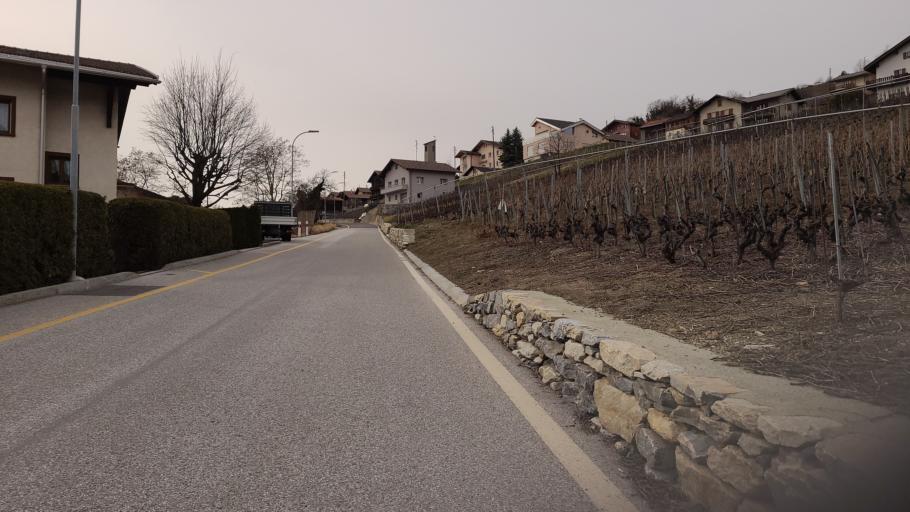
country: CH
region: Valais
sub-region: Sion District
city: Saint-Leonard
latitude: 46.2578
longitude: 7.4043
